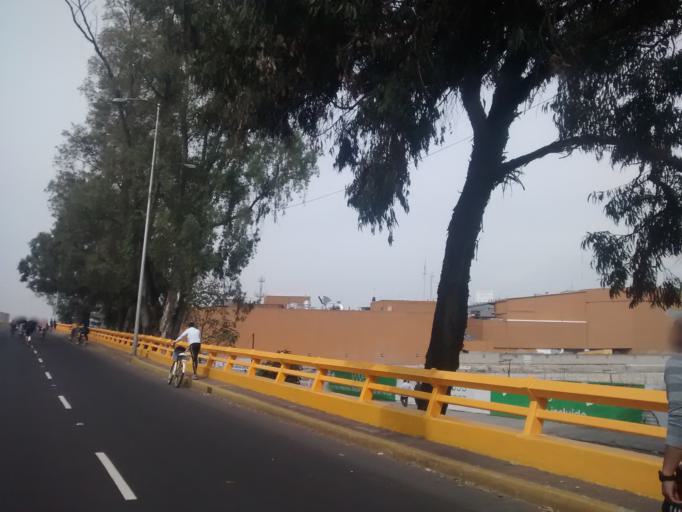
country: MX
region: Mexico City
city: Coyoacan
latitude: 19.3586
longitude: -99.1684
